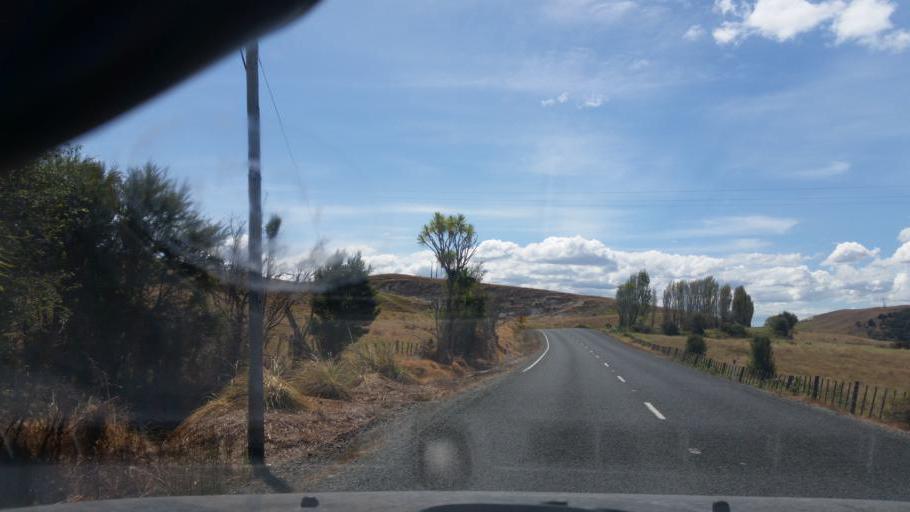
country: NZ
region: Northland
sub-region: Kaipara District
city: Dargaville
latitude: -36.1714
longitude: 174.1651
